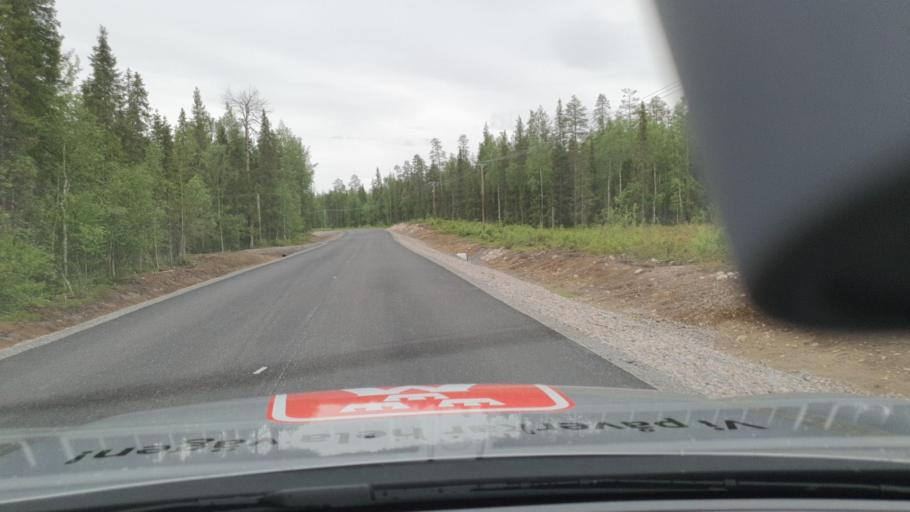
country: SE
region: Norrbotten
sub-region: Overkalix Kommun
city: OEverkalix
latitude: 66.6559
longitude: 23.2266
